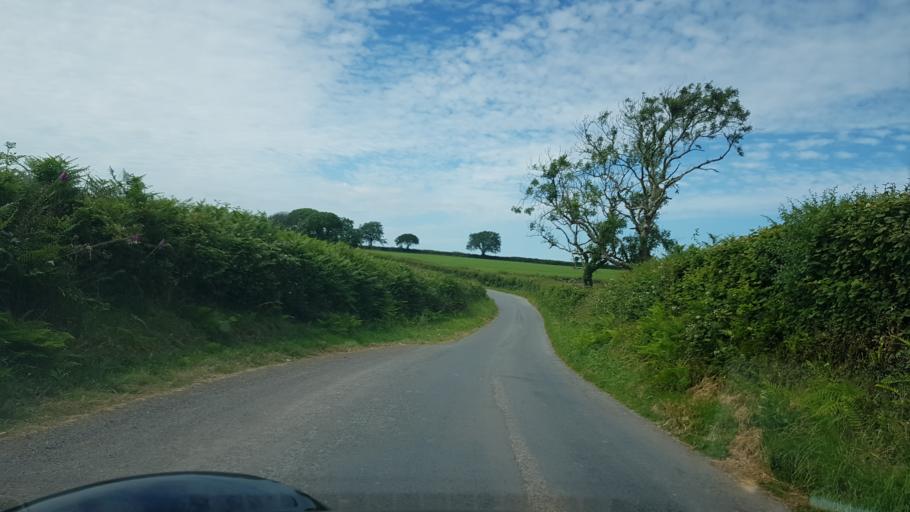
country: GB
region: Wales
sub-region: Carmarthenshire
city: Llanddowror
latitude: 51.7683
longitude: -4.5296
